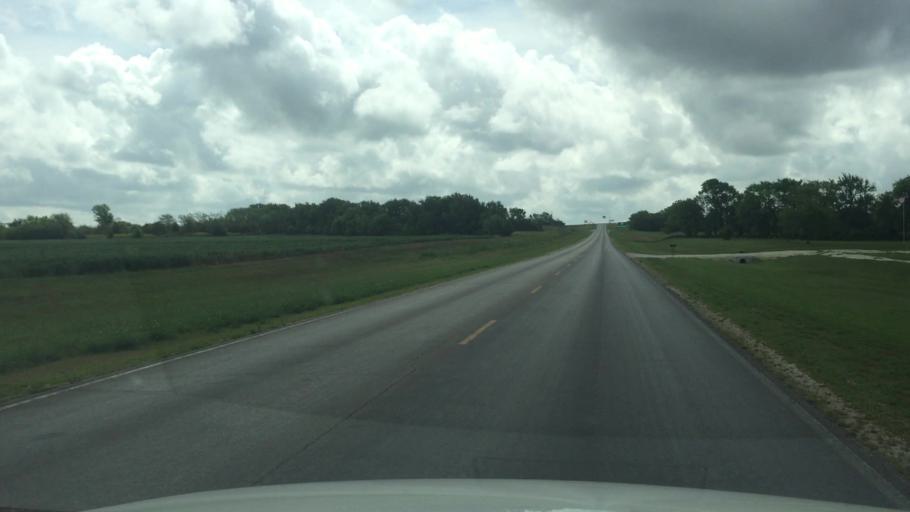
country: US
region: Kansas
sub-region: Allen County
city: Iola
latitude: 37.8873
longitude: -95.4053
